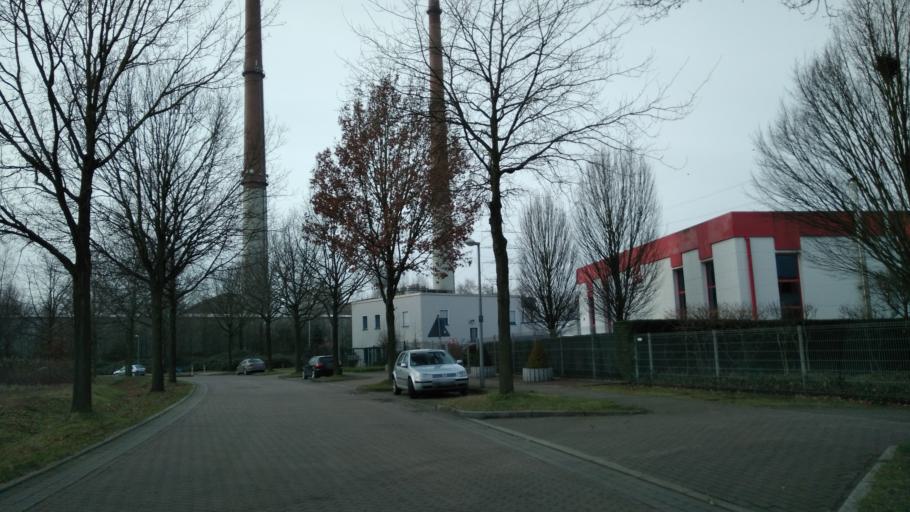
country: DE
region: North Rhine-Westphalia
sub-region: Regierungsbezirk Munster
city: Gladbeck
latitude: 51.5742
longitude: 6.9375
